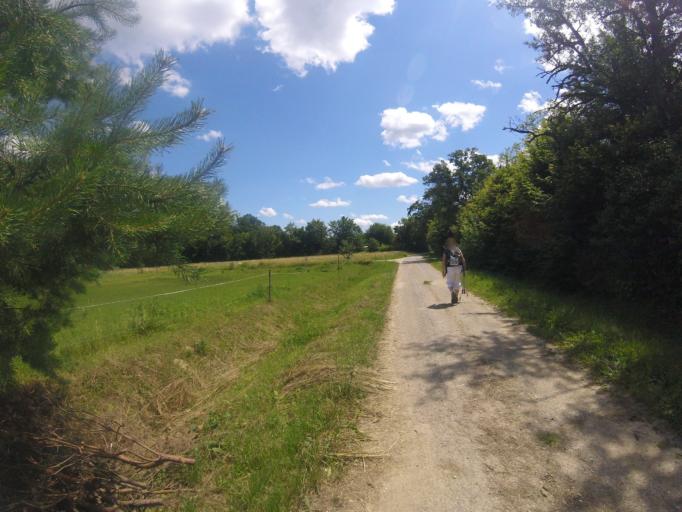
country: HU
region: Zala
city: Zalalovo
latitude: 46.8187
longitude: 16.5315
